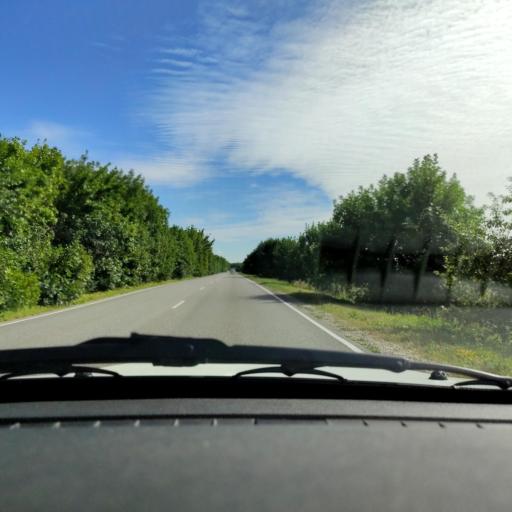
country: RU
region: Voronezj
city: Volya
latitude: 51.6966
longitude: 39.5074
